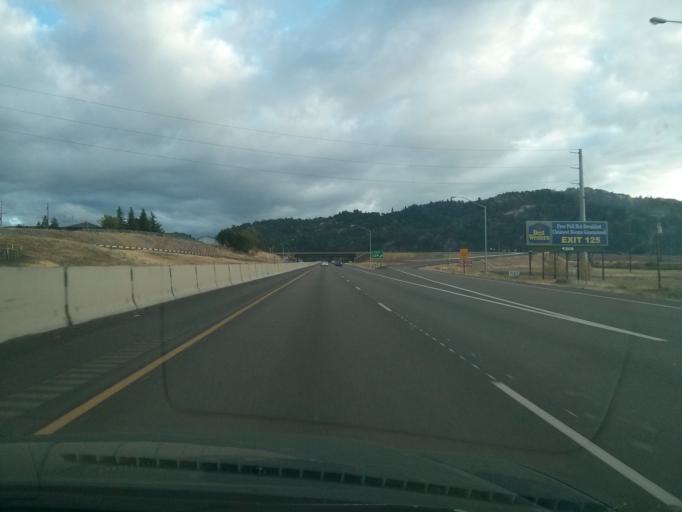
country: US
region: Oregon
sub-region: Douglas County
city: Roseburg North
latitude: 43.2943
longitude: -123.3523
